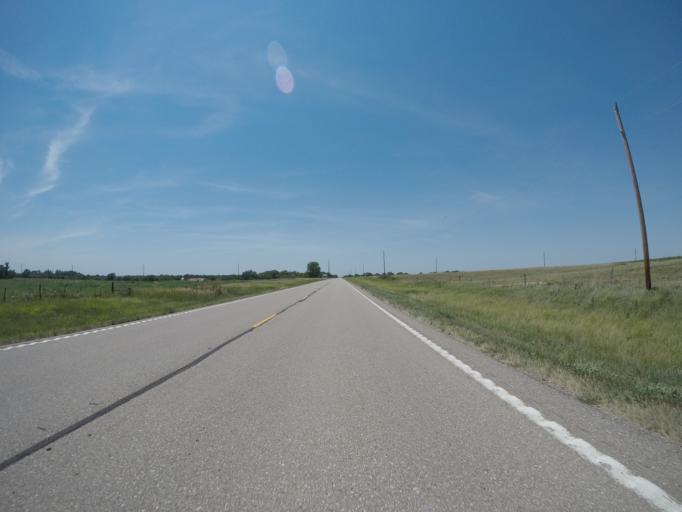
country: US
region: Kansas
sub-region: Dickinson County
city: Solomon
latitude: 39.0307
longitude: -97.5267
